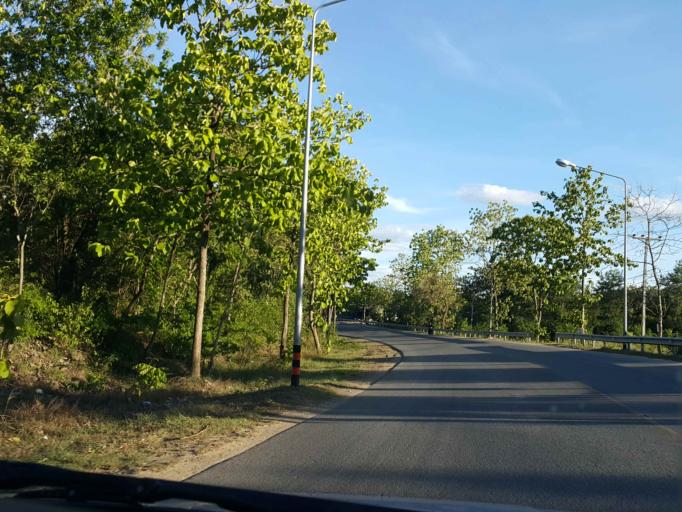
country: TH
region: Chiang Mai
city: Chom Thong
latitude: 18.4532
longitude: 98.6737
